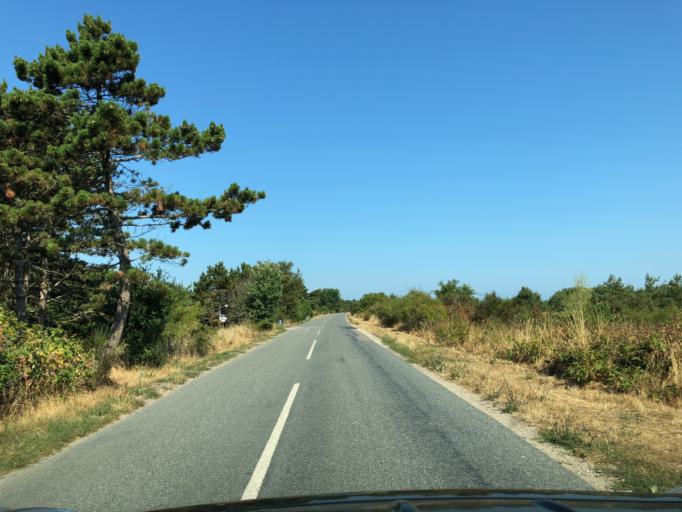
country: DK
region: Zealand
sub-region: Odsherred Kommune
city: Asnaes
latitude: 55.9917
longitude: 11.2948
